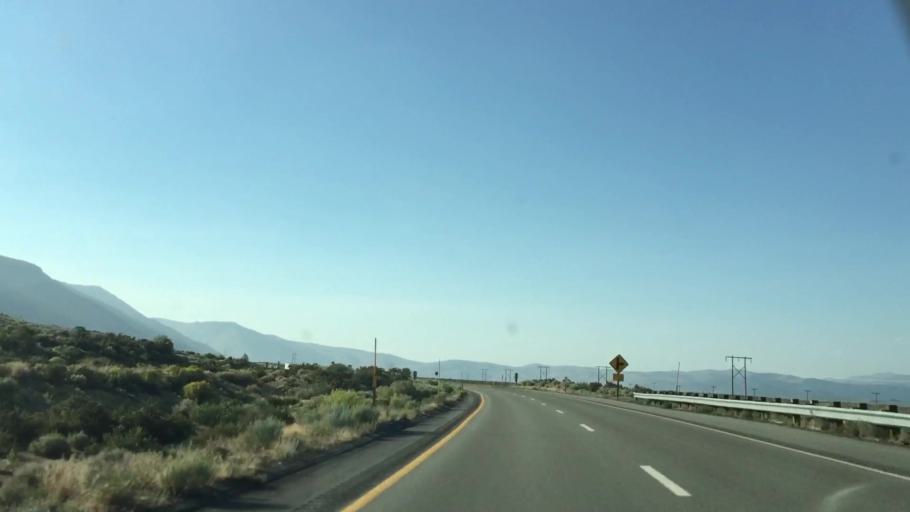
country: US
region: California
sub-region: Mono County
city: Mammoth Lakes
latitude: 37.9414
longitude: -119.1016
